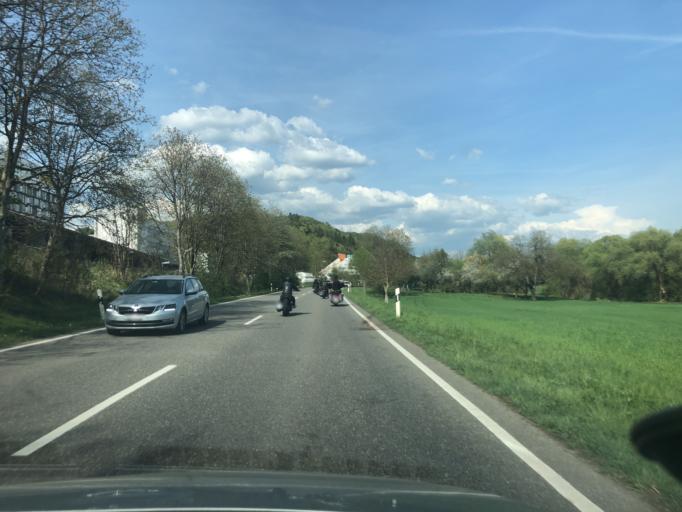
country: CH
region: Schaffhausen
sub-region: Bezirk Schleitheim
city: Schleitheim
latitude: 47.7641
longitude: 8.4711
